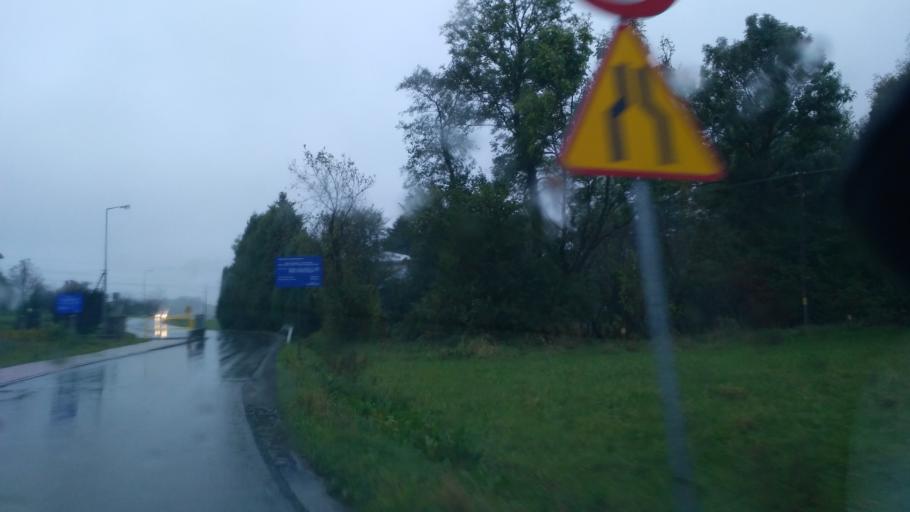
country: PL
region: Subcarpathian Voivodeship
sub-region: Powiat krosnienski
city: Korczyna
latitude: 49.7019
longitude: 21.8125
